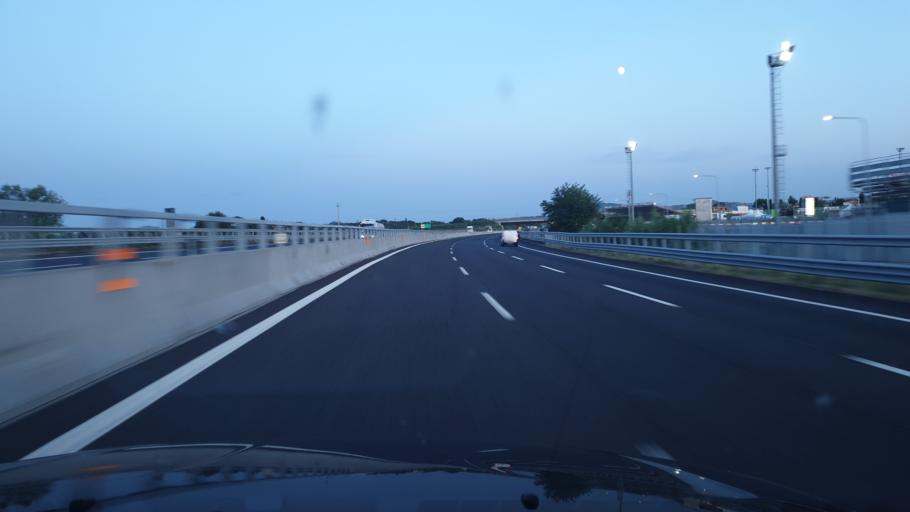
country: IT
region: Emilia-Romagna
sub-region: Provincia di Rimini
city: Santa Monica-Cella
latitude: 43.9670
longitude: 12.6858
